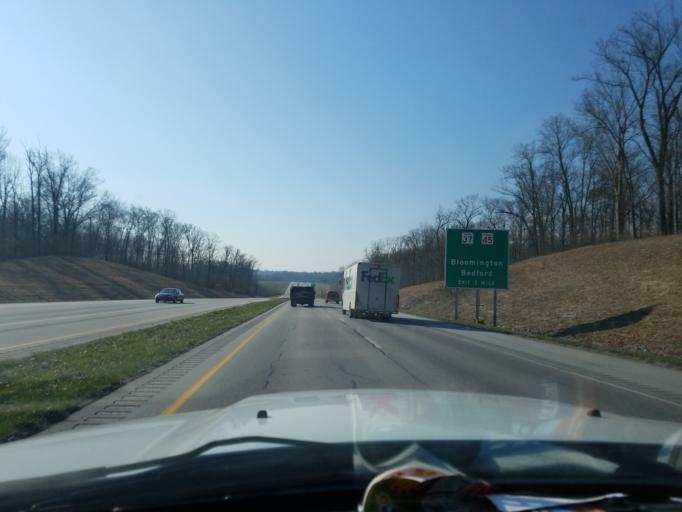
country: US
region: Indiana
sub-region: Monroe County
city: Ellettsville
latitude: 39.2016
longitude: -86.5762
